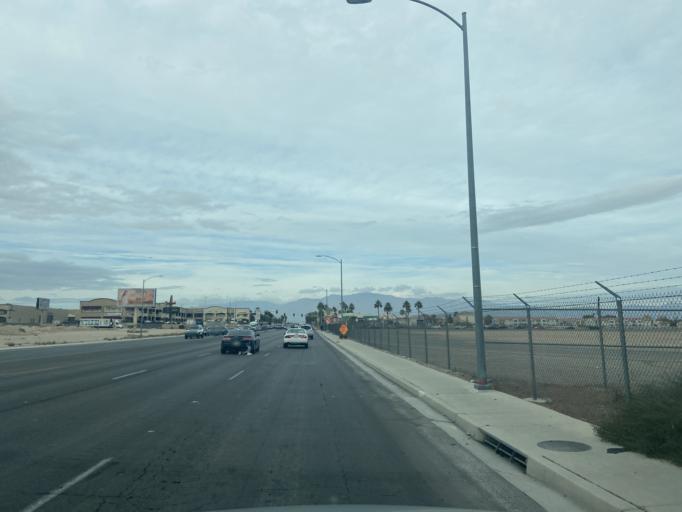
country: US
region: Nevada
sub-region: Clark County
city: Las Vegas
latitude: 36.2154
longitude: -115.2074
